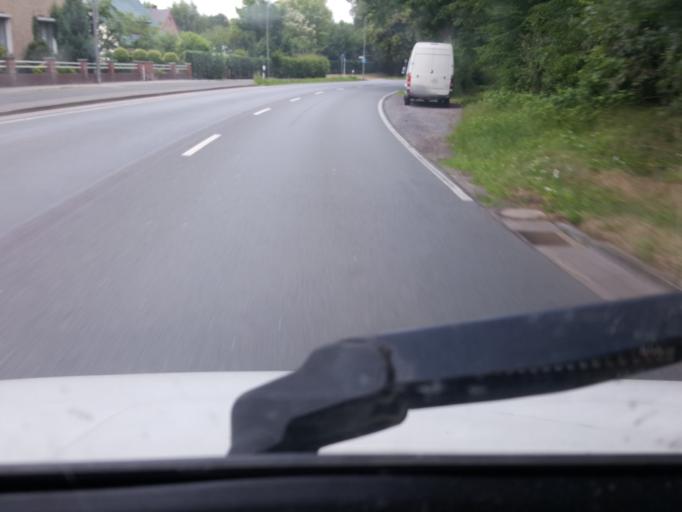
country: DE
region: North Rhine-Westphalia
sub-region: Regierungsbezirk Detmold
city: Minden
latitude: 52.3142
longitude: 8.9152
